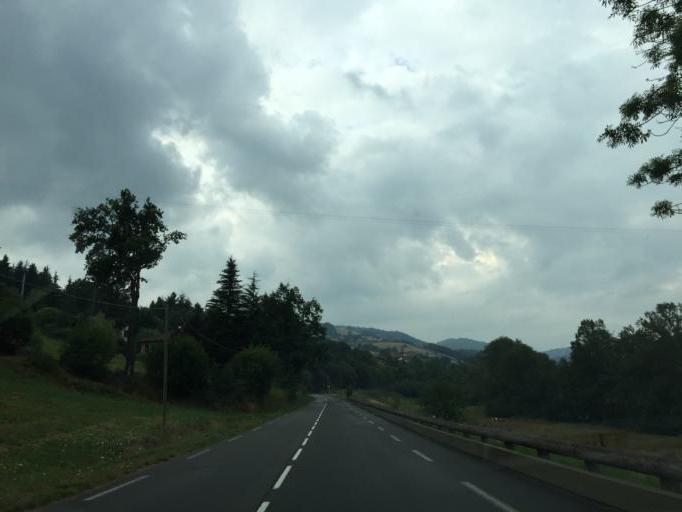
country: FR
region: Rhone-Alpes
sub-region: Departement de la Loire
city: Sorbiers
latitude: 45.5127
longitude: 4.4421
